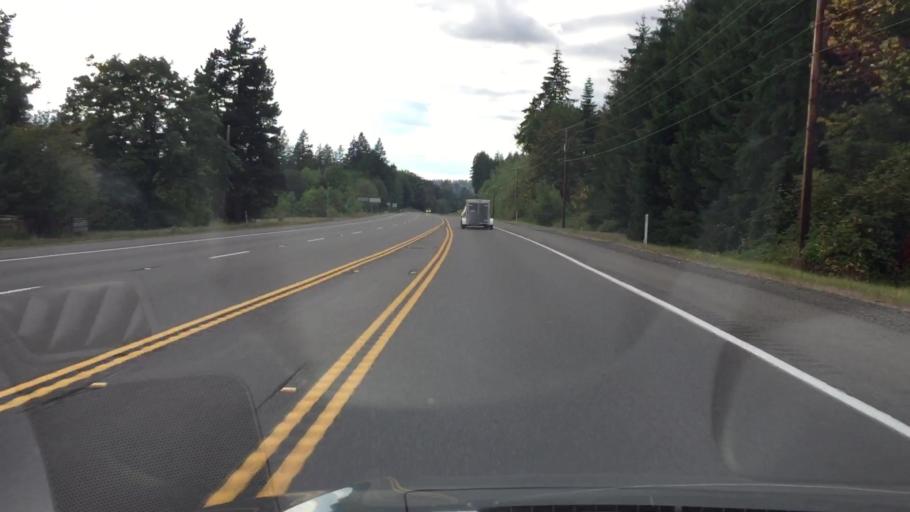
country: US
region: Washington
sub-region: Lewis County
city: Napavine
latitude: 46.5264
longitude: -122.5977
